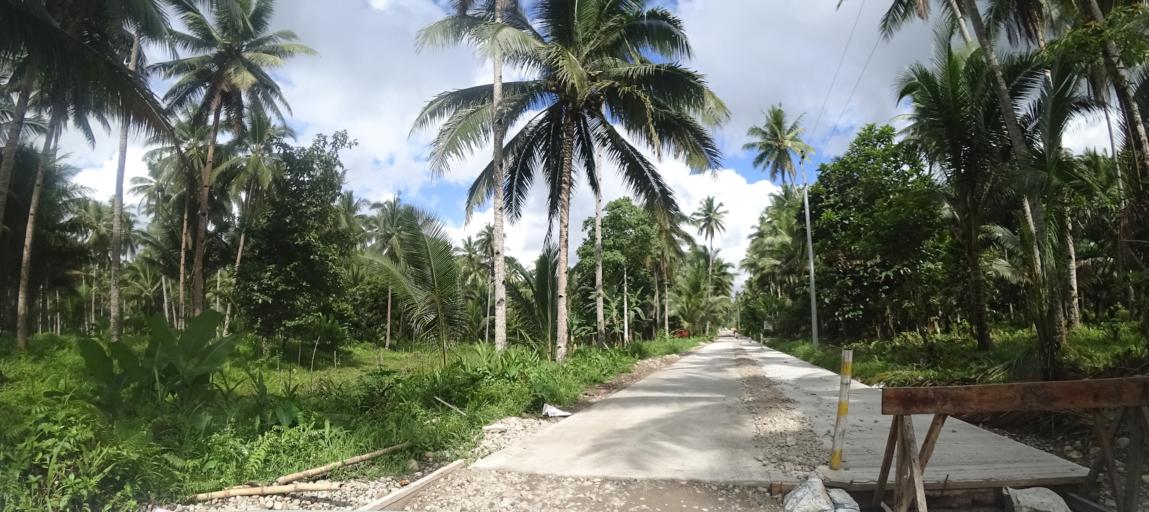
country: PH
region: Eastern Visayas
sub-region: Province of Leyte
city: Bugho
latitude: 10.8261
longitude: 124.9203
